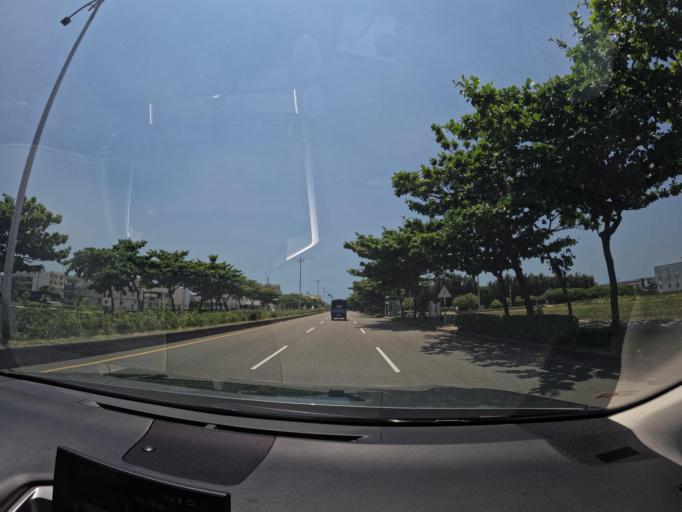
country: TW
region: Taiwan
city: Fengyuan
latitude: 24.2534
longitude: 120.5502
